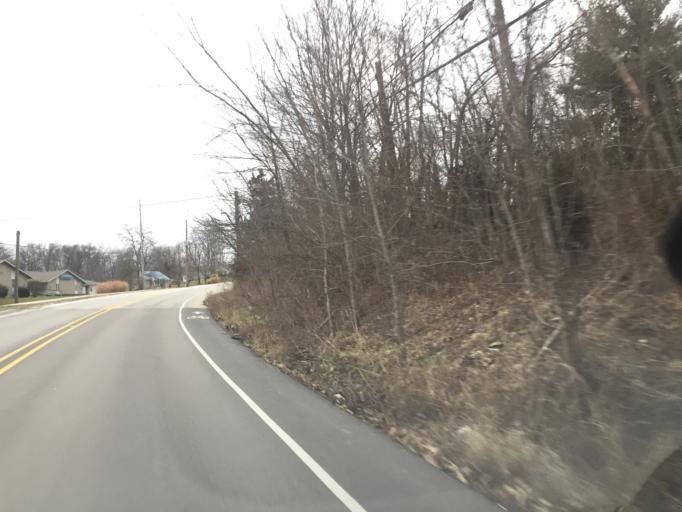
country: US
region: Indiana
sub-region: Monroe County
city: Bloomington
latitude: 39.1798
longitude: -86.5482
